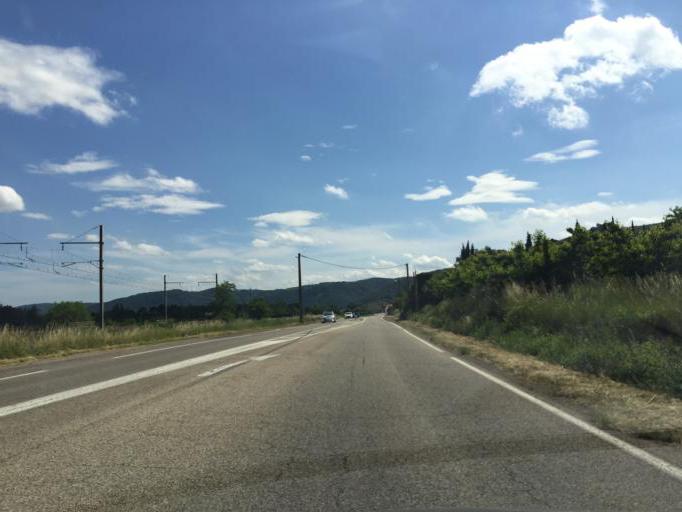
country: FR
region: Rhone-Alpes
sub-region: Departement de la Drome
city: Saint-Vallier
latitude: 45.1493
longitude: 4.8133
